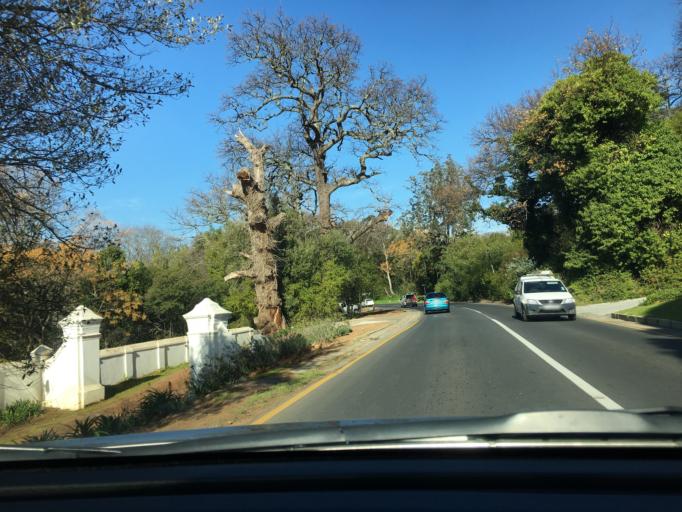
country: ZA
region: Western Cape
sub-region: City of Cape Town
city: Constantia
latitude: -34.0197
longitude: 18.4194
